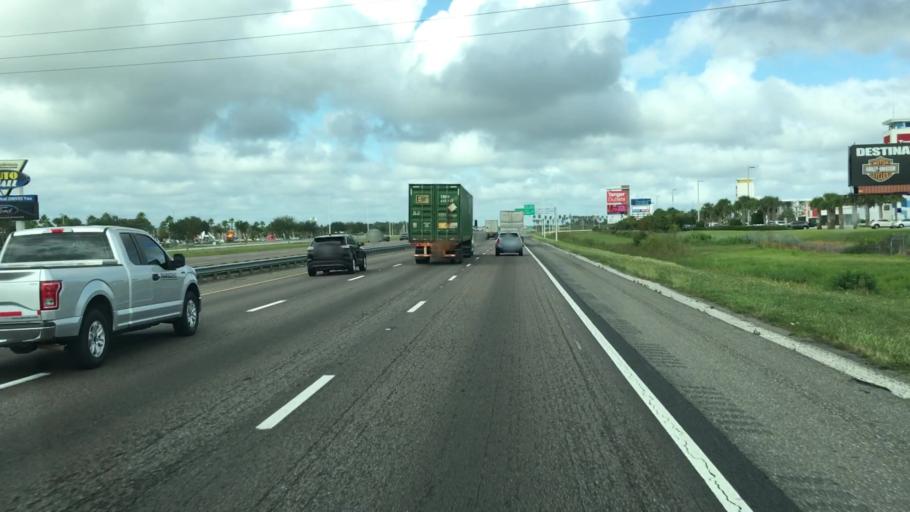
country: US
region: Florida
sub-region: Volusia County
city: Holly Hill
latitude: 29.2104
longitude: -81.0997
